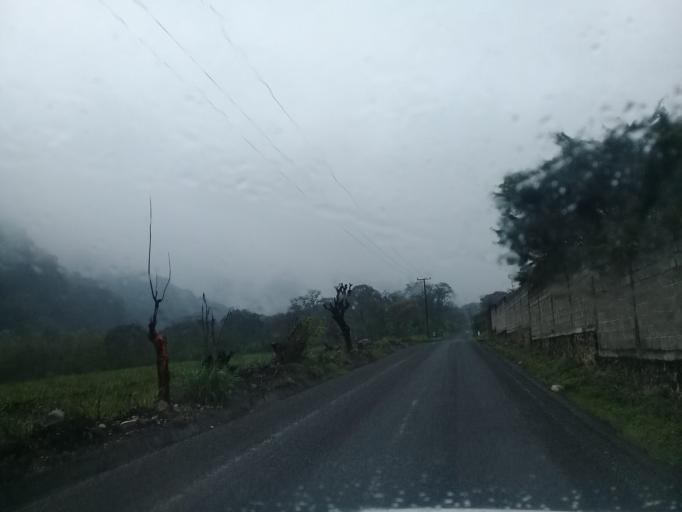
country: MX
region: Veracruz
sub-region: Amatlan de los Reyes
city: Centro de Readaptacion Social
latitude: 18.7988
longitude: -96.9364
